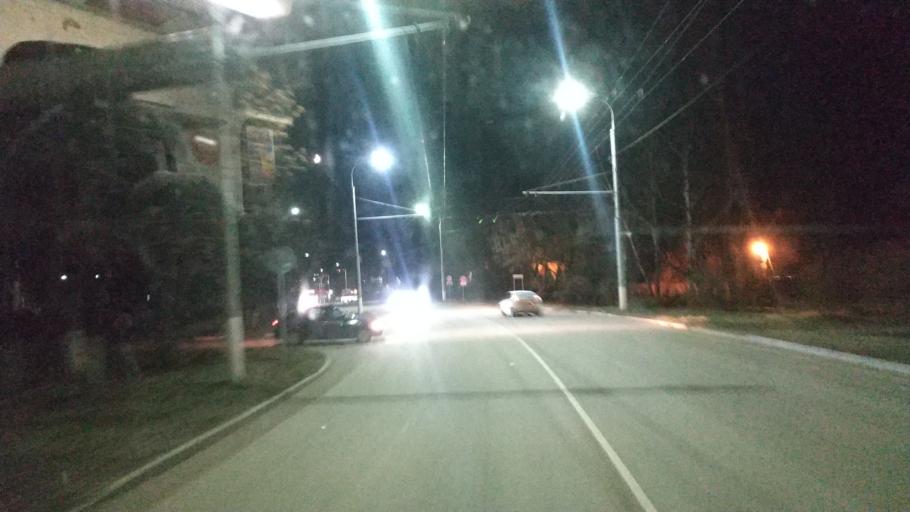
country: RU
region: Moskovskaya
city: Dubrovitsy
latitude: 55.4344
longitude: 37.4957
